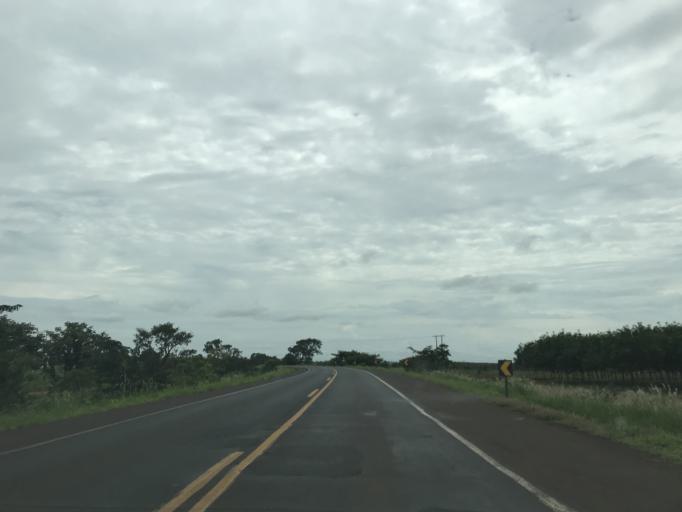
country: BR
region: Minas Gerais
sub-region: Frutal
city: Frutal
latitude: -20.0519
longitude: -49.0531
